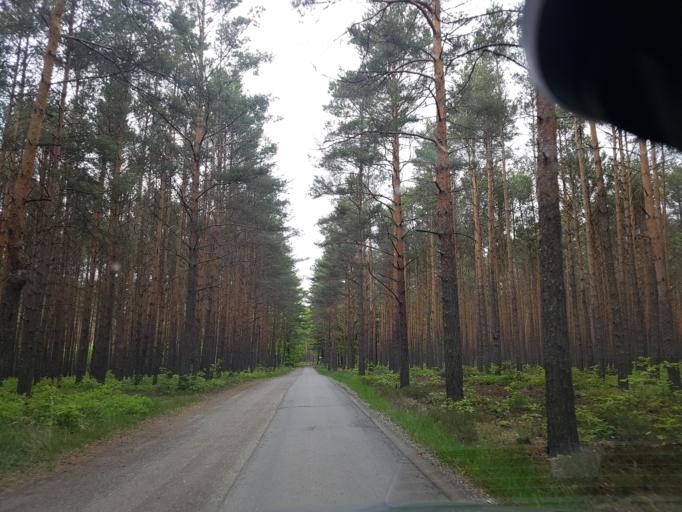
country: DE
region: Brandenburg
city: Crinitz
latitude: 51.6975
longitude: 13.7746
